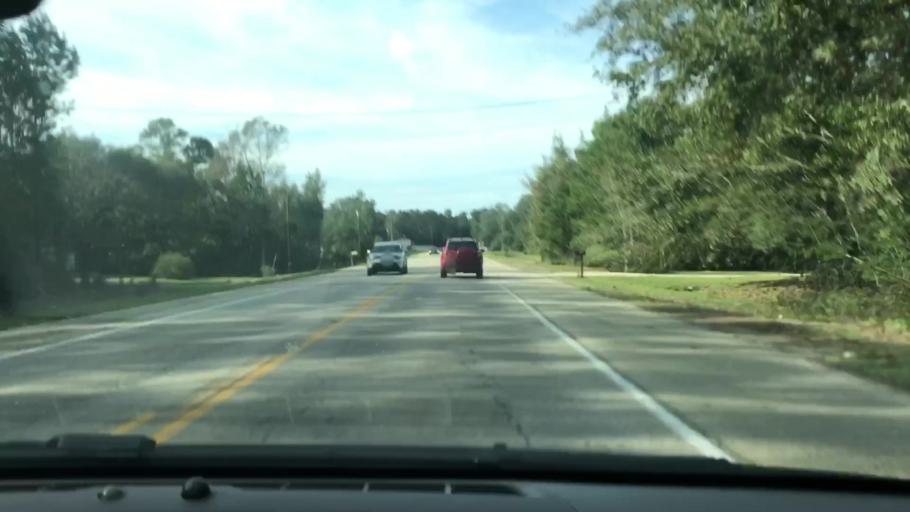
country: US
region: Louisiana
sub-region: Saint Tammany Parish
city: Pearl River
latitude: 30.4635
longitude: -89.8096
